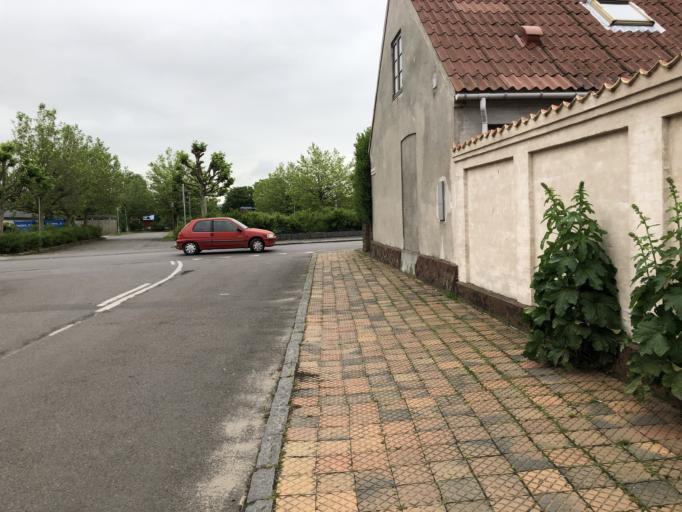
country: DK
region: Capital Region
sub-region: Bornholm Kommune
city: Ronne
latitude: 55.1013
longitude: 14.7070
